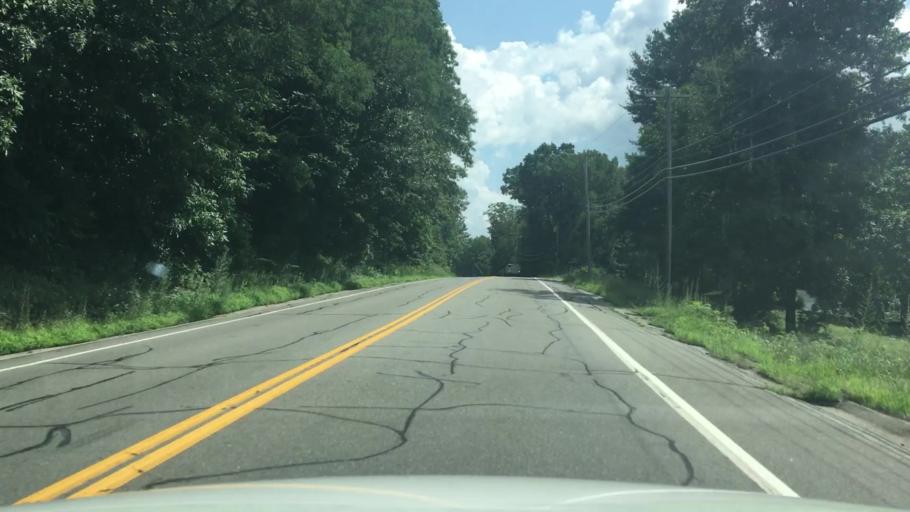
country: US
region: New Hampshire
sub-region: Rockingham County
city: Auburn
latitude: 42.9760
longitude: -71.3681
